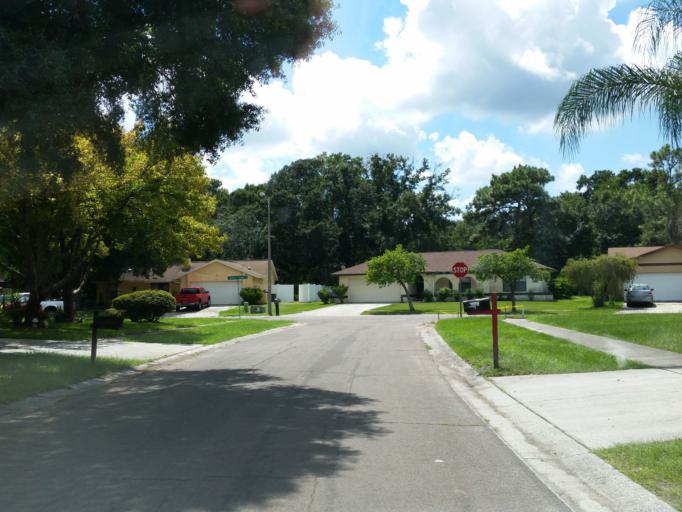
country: US
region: Florida
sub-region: Hillsborough County
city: Bloomingdale
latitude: 27.8764
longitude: -82.2711
